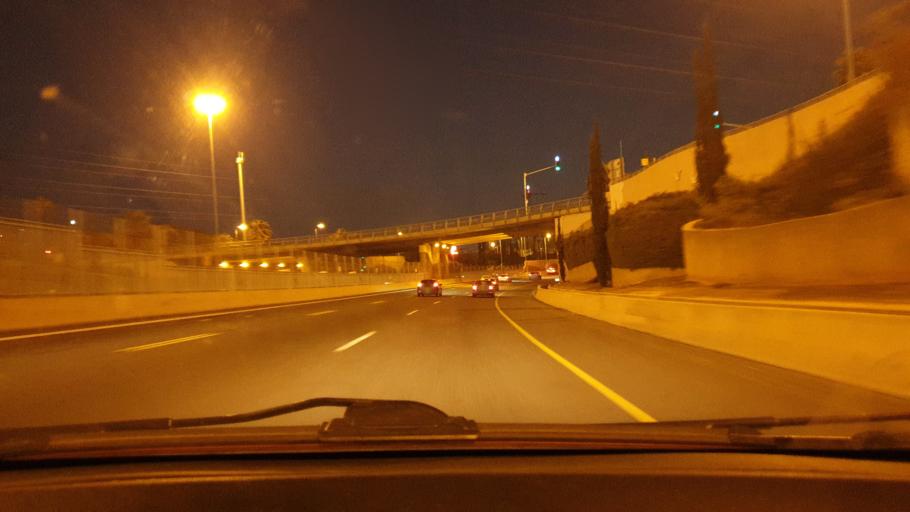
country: IL
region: Tel Aviv
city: Bat Yam
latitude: 32.0360
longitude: 34.7601
